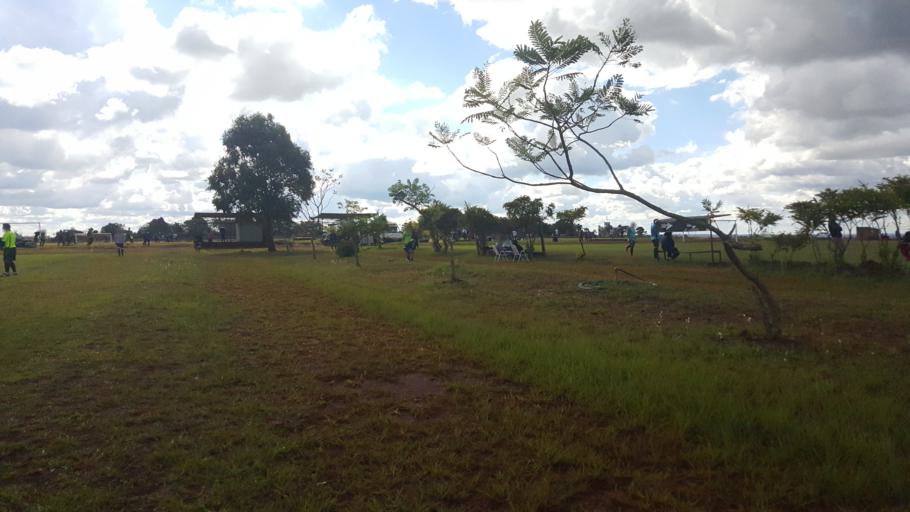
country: AR
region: Misiones
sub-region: Departamento de Capital
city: Posadas
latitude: -27.4154
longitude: -56.0066
